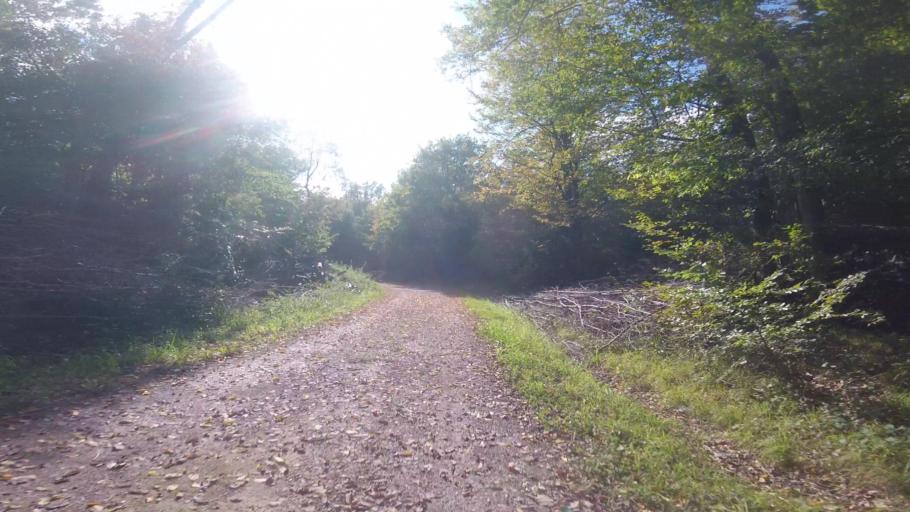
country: DE
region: Baden-Wuerttemberg
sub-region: Regierungsbezirk Stuttgart
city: Kirchberg an der Murr
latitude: 48.9858
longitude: 9.3365
